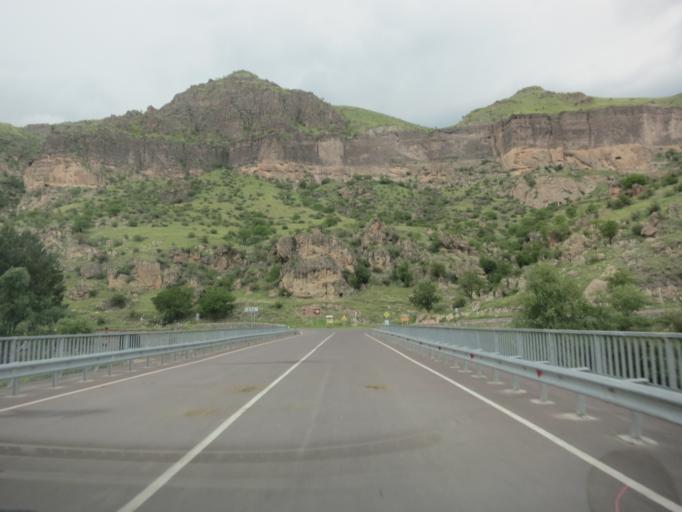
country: TR
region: Ardahan
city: Kurtkale
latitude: 41.3772
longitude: 43.2814
